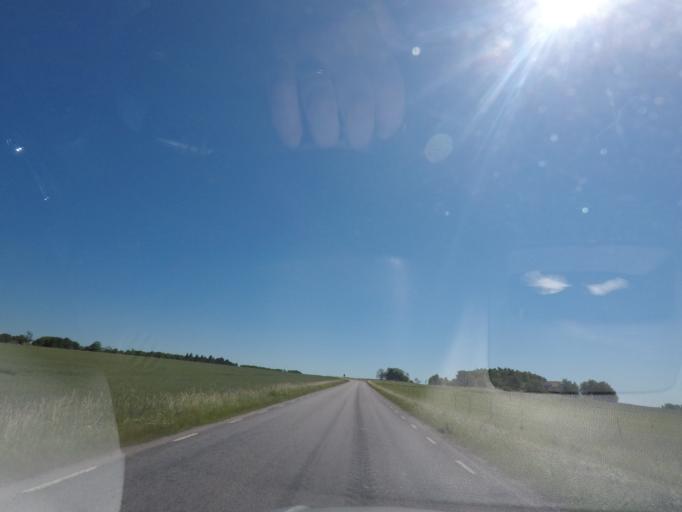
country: SE
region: Uppsala
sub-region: Enkopings Kommun
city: Irsta
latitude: 59.6797
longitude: 16.8446
